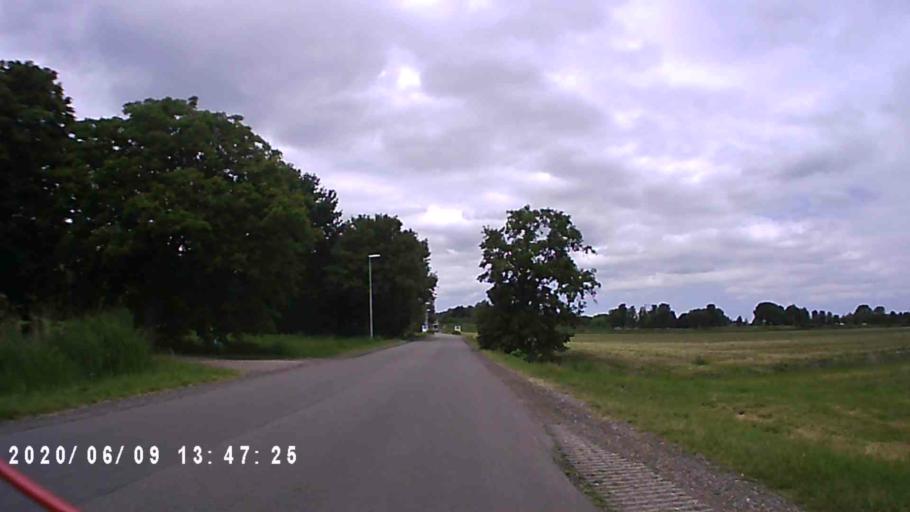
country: NL
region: Groningen
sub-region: Gemeente Groningen
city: Oosterpark
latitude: 53.2269
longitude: 6.6332
